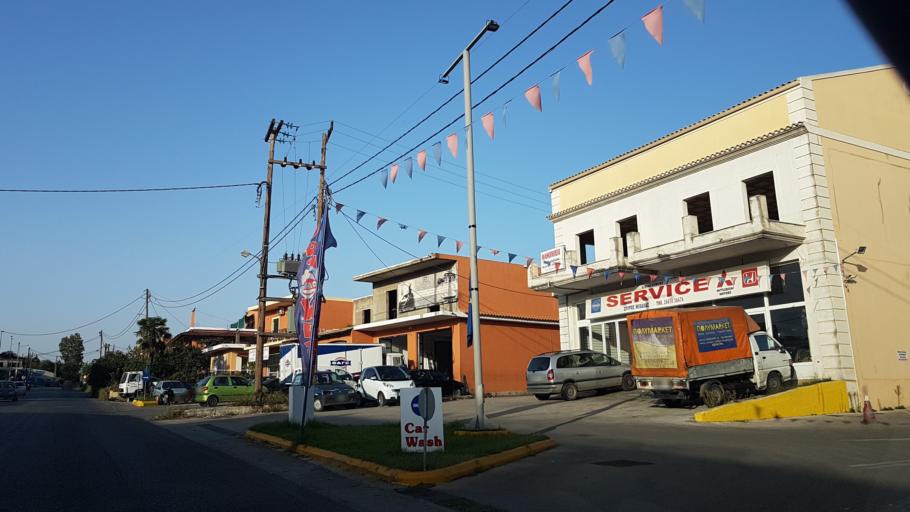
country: GR
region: Ionian Islands
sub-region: Nomos Kerkyras
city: Kanali
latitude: 39.6001
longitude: 19.8940
